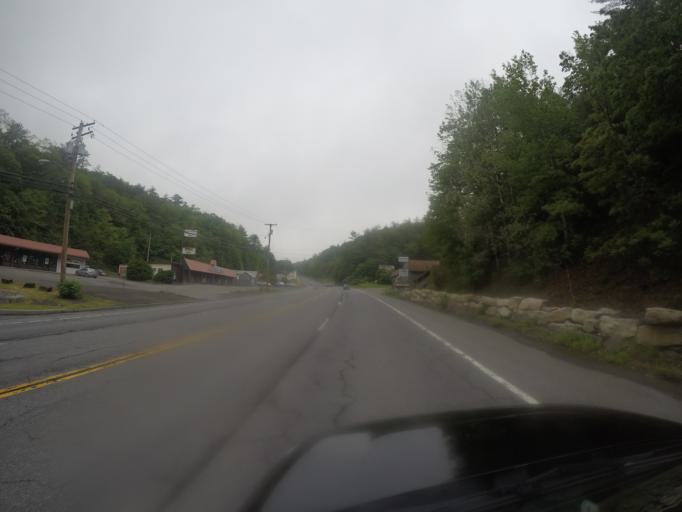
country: US
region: New York
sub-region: Ulster County
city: Hurley
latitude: 41.9687
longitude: -74.0698
